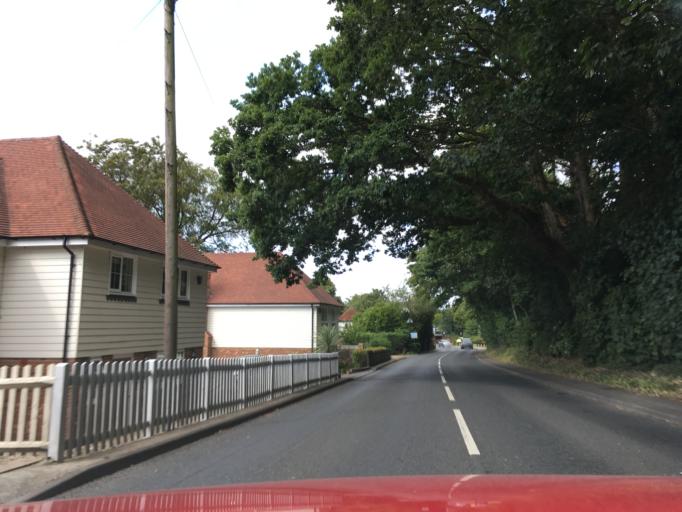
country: GB
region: England
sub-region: Kent
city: Tenterden
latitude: 51.0780
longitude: 0.6953
